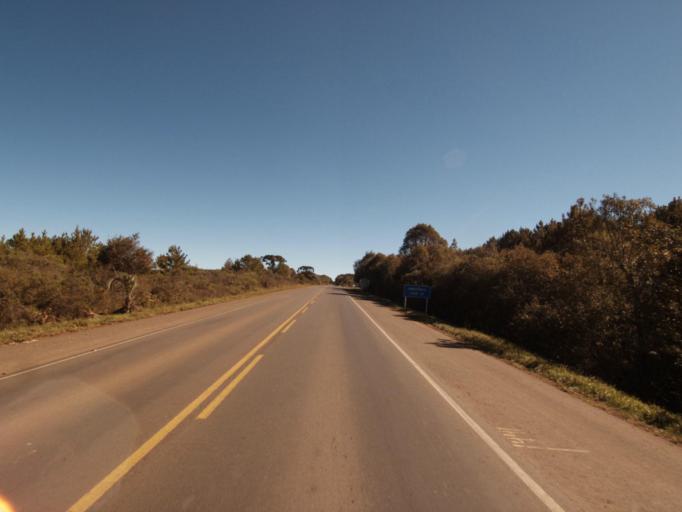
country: BR
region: Santa Catarina
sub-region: Concordia
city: Concordia
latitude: -26.9168
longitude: -51.8948
